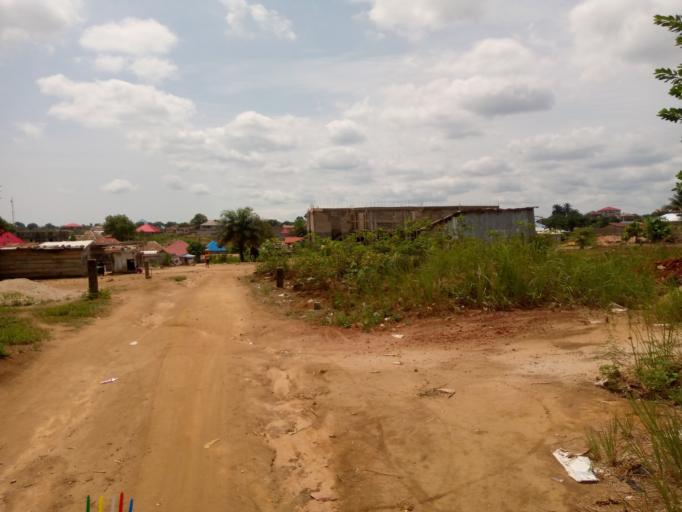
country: SL
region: Western Area
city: Waterloo
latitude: 8.3303
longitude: -13.0335
